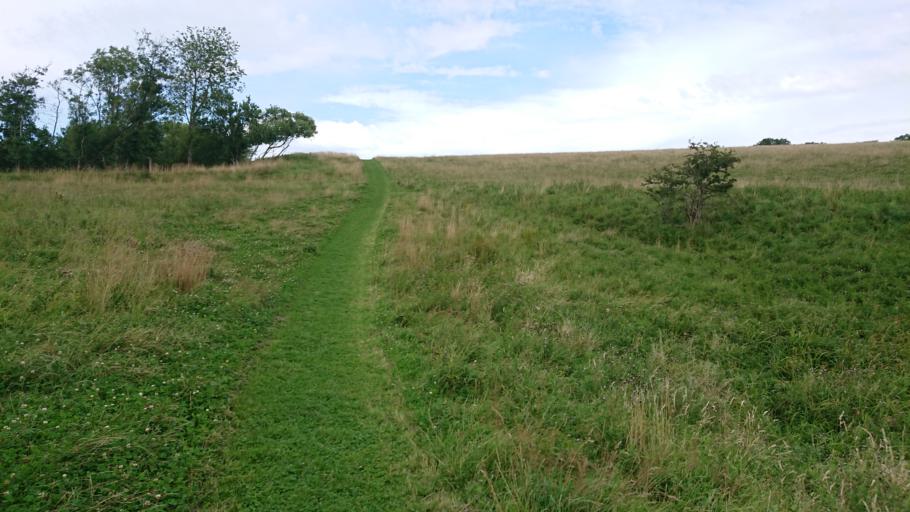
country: DK
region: North Denmark
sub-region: Hjorring Kommune
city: Sindal
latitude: 57.4801
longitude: 10.1560
